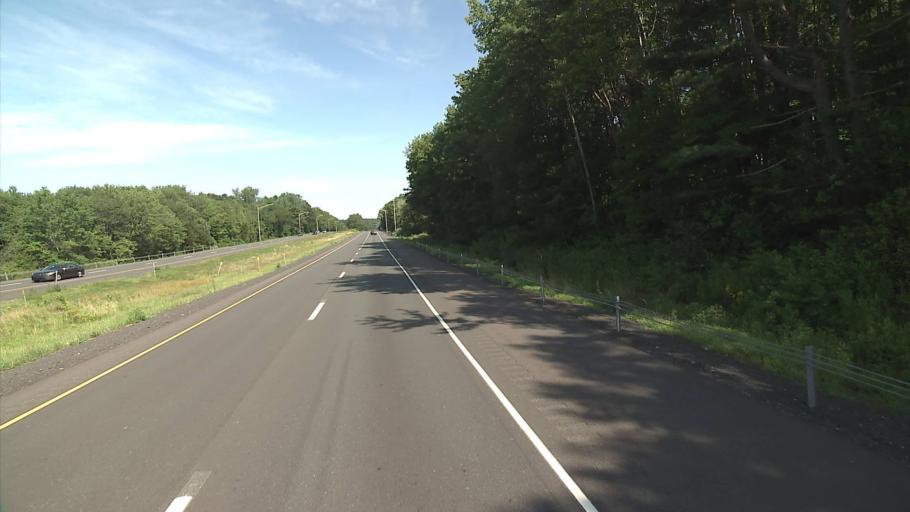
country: US
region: Connecticut
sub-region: Hartford County
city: Glastonbury Center
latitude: 41.6695
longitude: -72.5344
